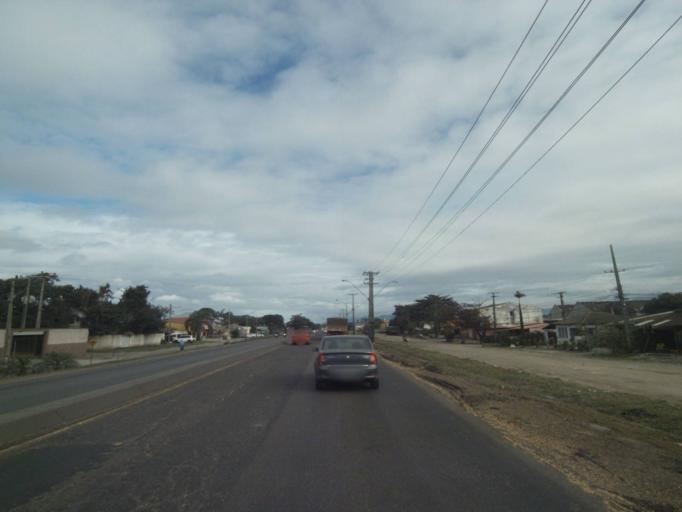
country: BR
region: Parana
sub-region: Paranagua
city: Paranagua
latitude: -25.5294
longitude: -48.5285
